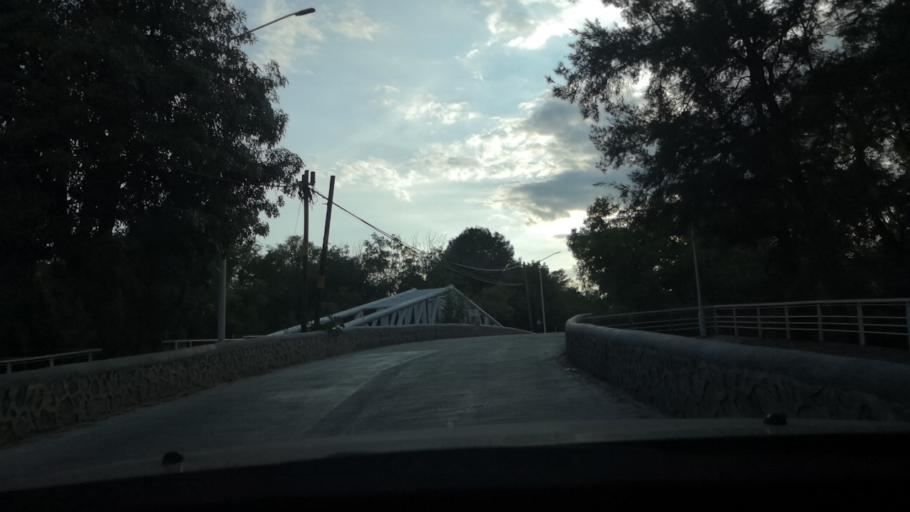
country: MX
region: Guanajuato
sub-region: San Francisco del Rincon
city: Estacion de San Francisco
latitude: 21.0266
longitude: -101.8347
